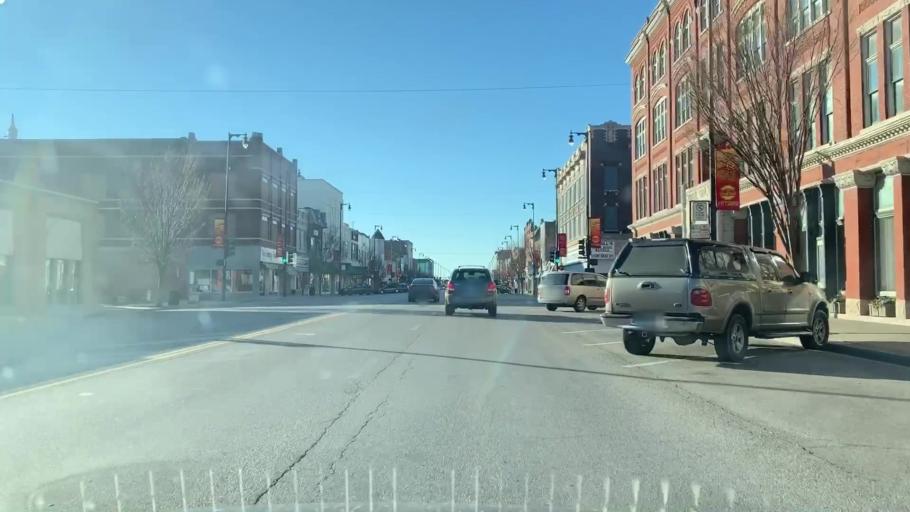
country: US
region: Kansas
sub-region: Crawford County
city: Pittsburg
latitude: 37.4146
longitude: -94.7049
